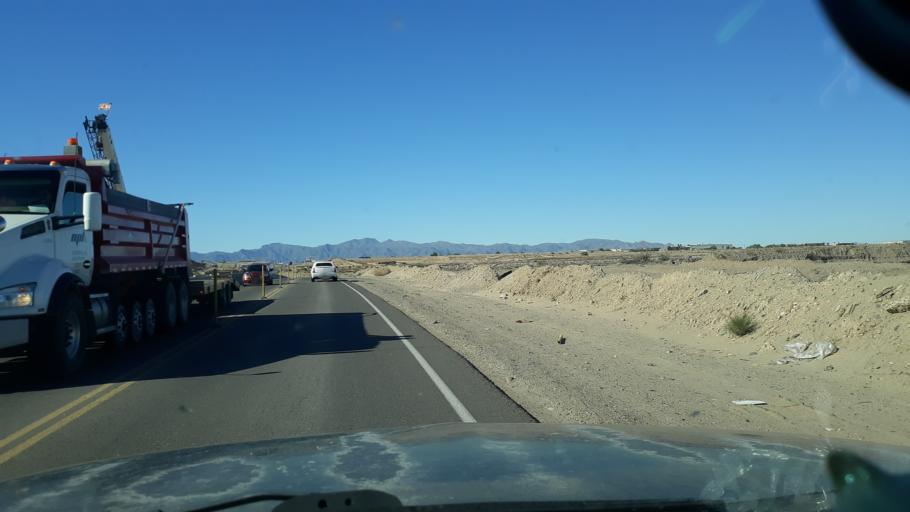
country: US
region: Arizona
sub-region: Maricopa County
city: Youngtown
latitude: 33.5512
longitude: -112.3139
